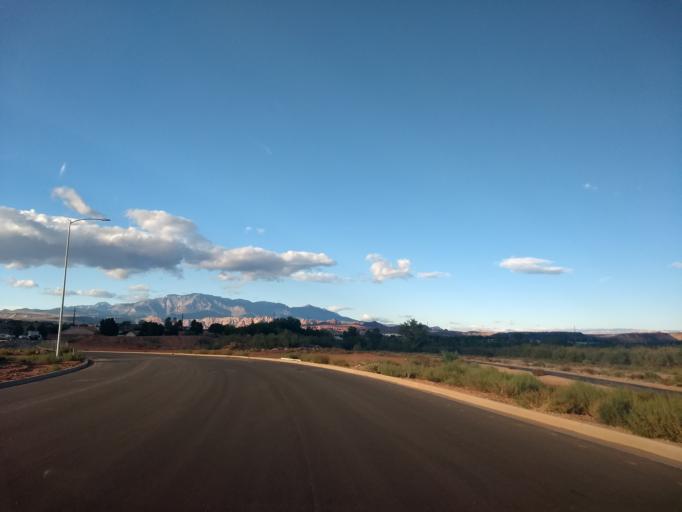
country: US
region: Utah
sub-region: Washington County
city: Washington
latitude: 37.1012
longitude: -113.5291
